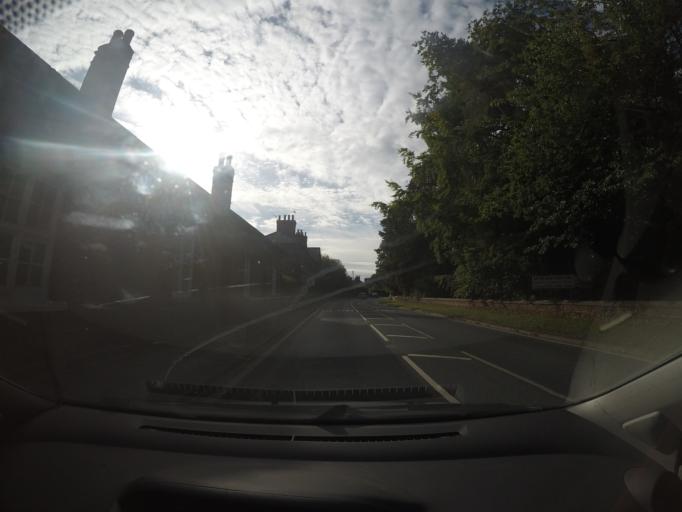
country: GB
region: England
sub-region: City of York
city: Deighton
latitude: 53.8803
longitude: -1.0449
